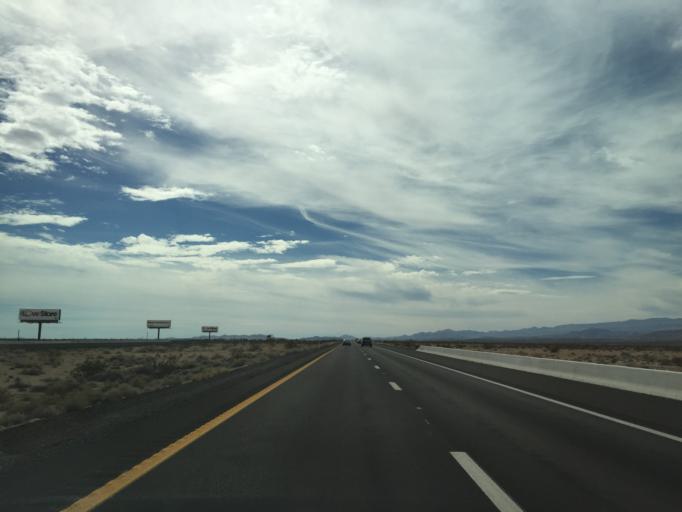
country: US
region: Nevada
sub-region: Clark County
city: Moapa Town
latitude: 36.5775
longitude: -114.6608
